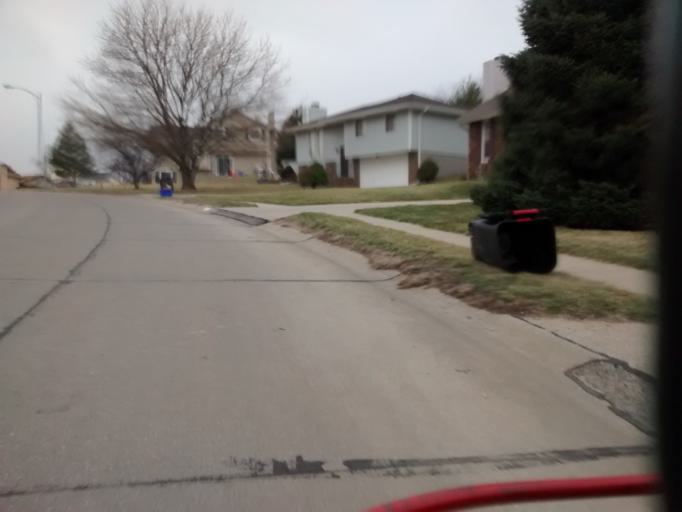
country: US
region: Nebraska
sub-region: Sarpy County
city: Offutt Air Force Base
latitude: 41.1636
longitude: -95.9293
